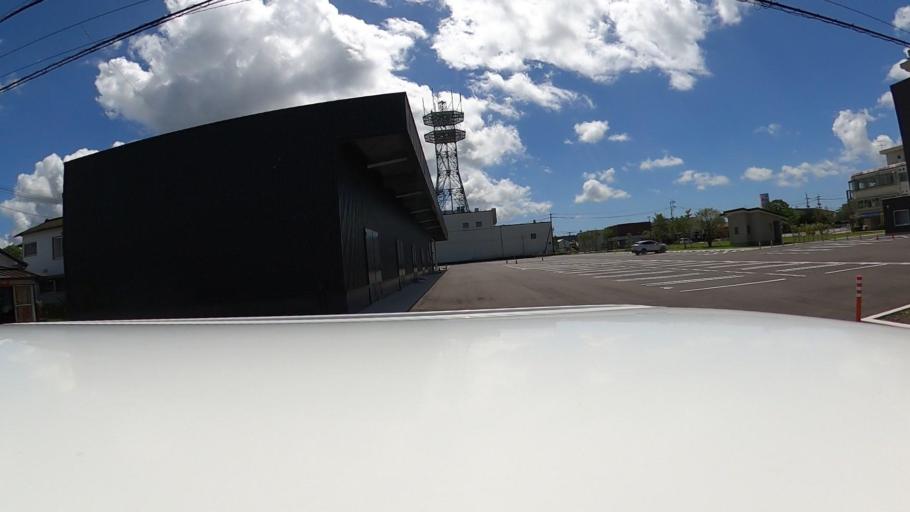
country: JP
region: Miyazaki
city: Tsuma
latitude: 32.1091
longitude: 131.4009
